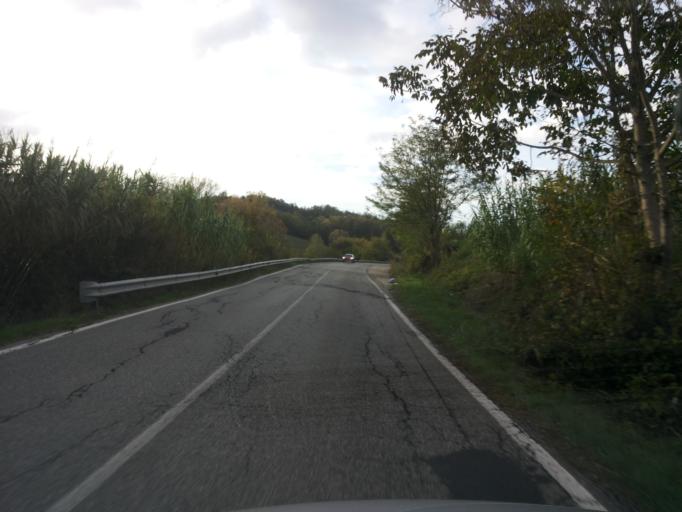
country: IT
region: Piedmont
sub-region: Provincia di Alessandria
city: San Giorgio
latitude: 45.1036
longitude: 8.3979
